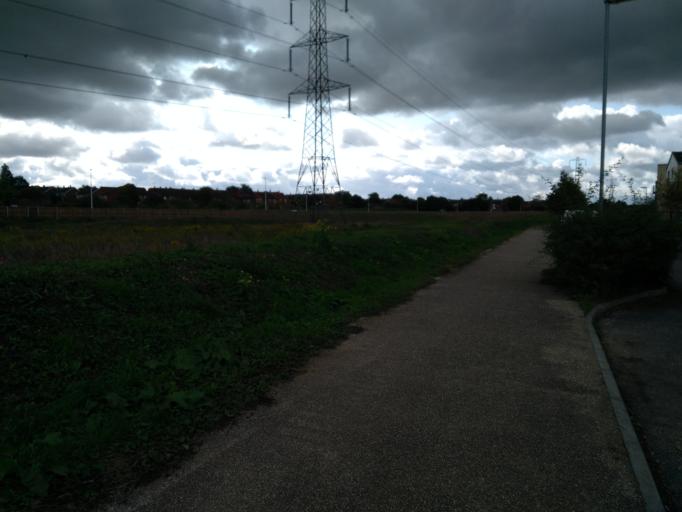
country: GB
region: England
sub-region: Central Bedfordshire
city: Houghton Regis
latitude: 51.9054
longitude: -0.4991
